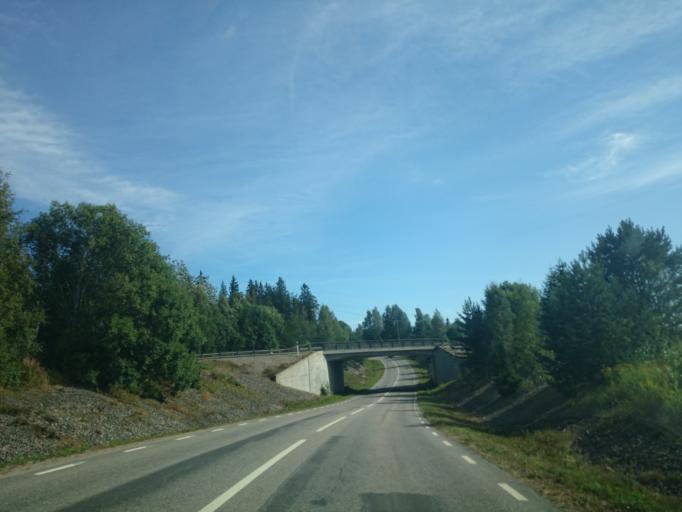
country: SE
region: Gaevleborg
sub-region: Hudiksvalls Kommun
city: Hudiksvall
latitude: 61.7551
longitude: 17.0838
